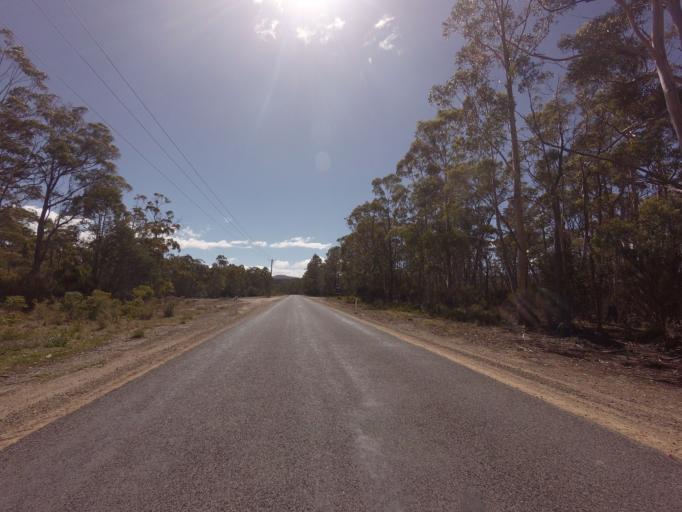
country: AU
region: Tasmania
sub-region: Break O'Day
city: St Helens
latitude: -41.5971
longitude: 148.2040
